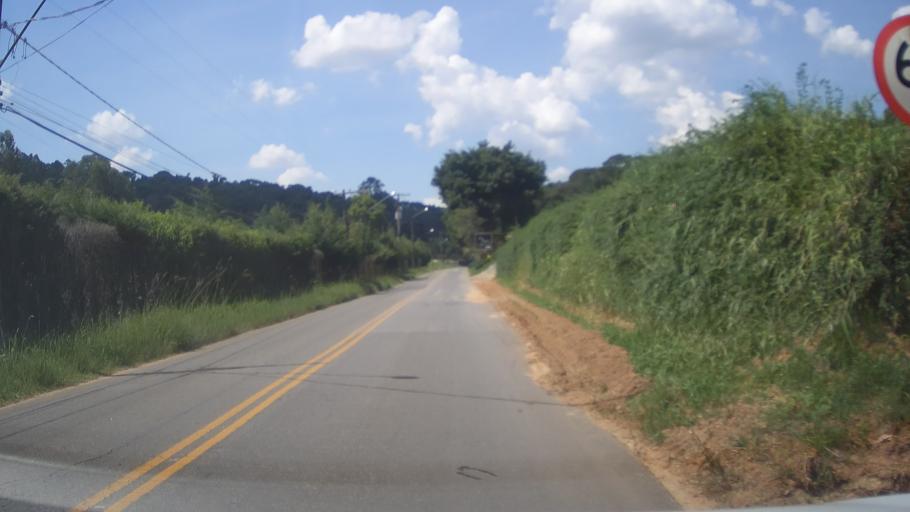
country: BR
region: Sao Paulo
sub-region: Jundiai
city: Jundiai
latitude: -23.1423
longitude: -46.8311
